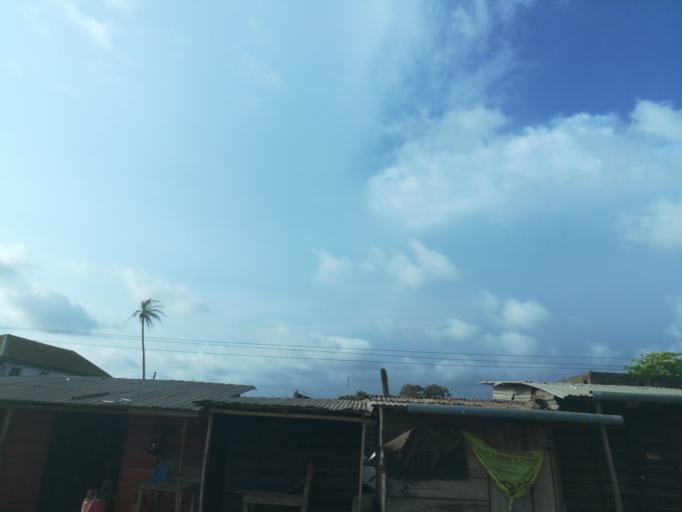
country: NG
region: Ogun
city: Ado Odo
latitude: 6.4815
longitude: 3.0281
